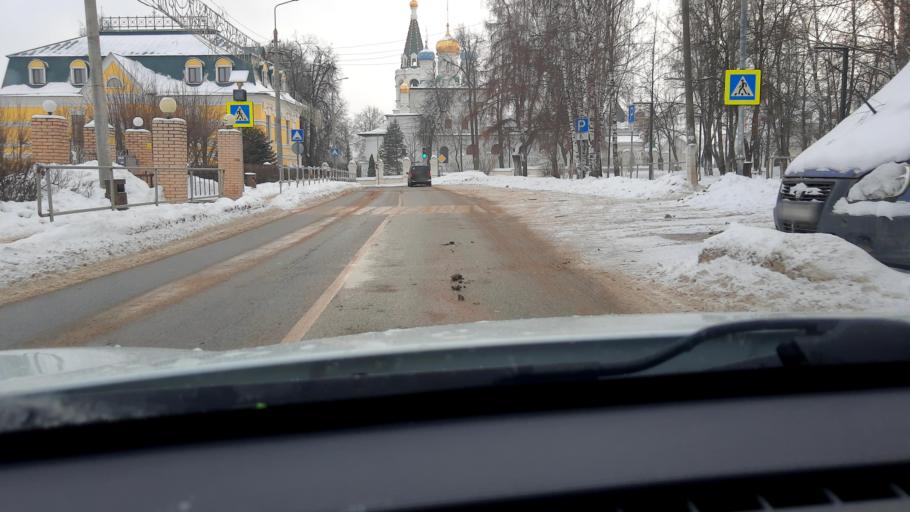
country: RU
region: Moskovskaya
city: Pavlovskaya Sloboda
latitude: 55.8160
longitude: 37.0902
